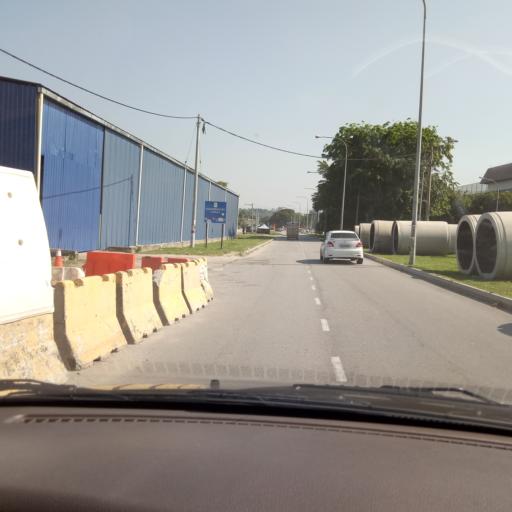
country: MY
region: Selangor
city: Kampong Baharu Balakong
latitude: 3.0215
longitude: 101.7653
